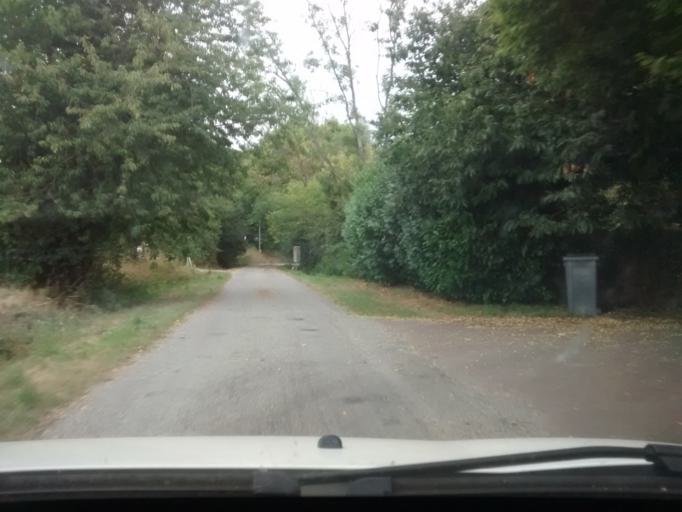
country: FR
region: Brittany
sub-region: Departement d'Ille-et-Vilaine
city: Cesson-Sevigne
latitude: 48.1020
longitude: -1.5955
